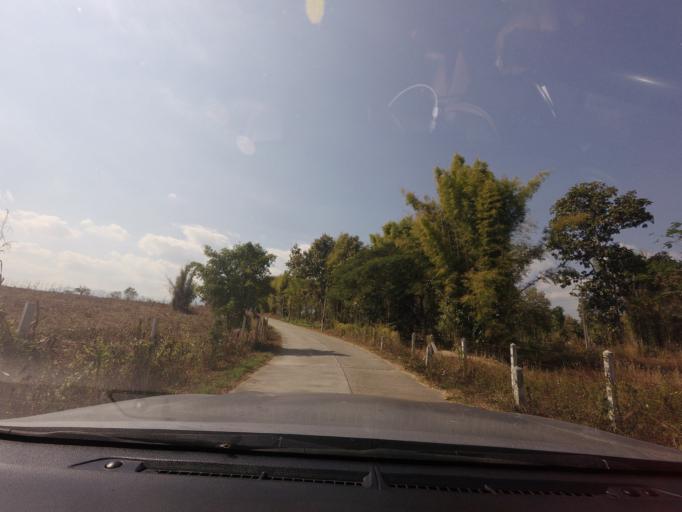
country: TH
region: Mae Hong Son
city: Wiang Nuea
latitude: 19.3844
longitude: 98.4332
